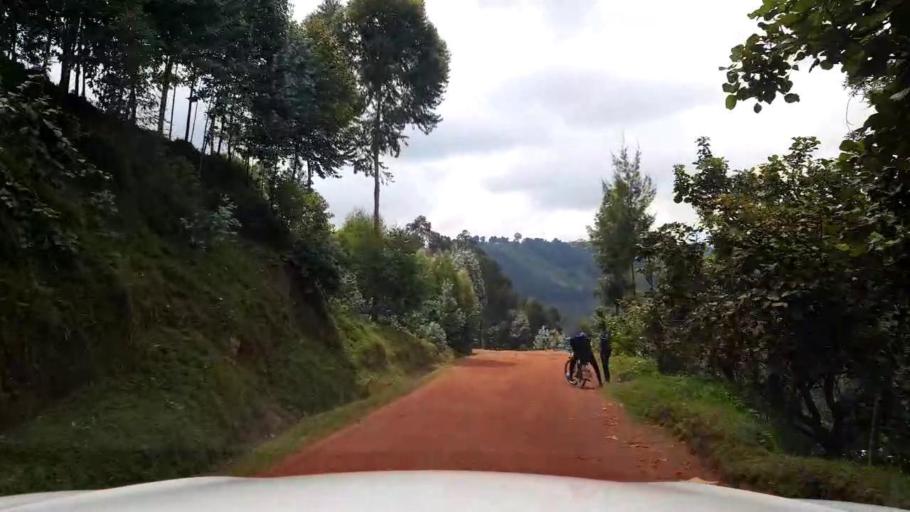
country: UG
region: Western Region
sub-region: Kisoro District
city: Kisoro
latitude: -1.4172
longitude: 29.8286
